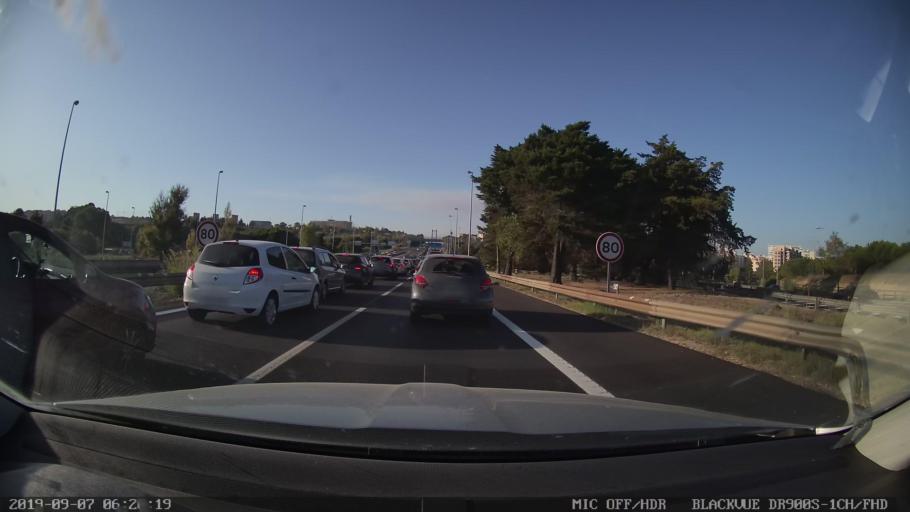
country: PT
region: Setubal
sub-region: Almada
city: Pragal
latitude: 38.6629
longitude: -9.1734
